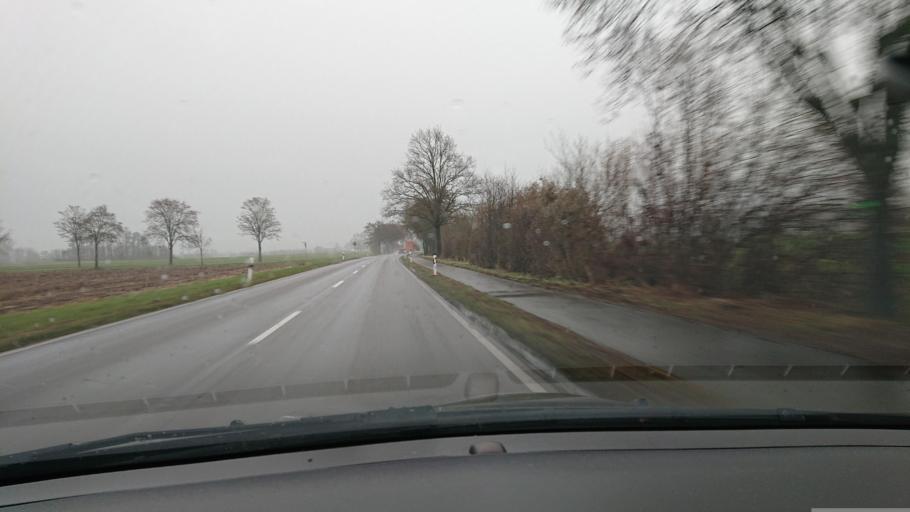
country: DE
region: North Rhine-Westphalia
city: Oelde
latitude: 51.8492
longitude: 8.1896
